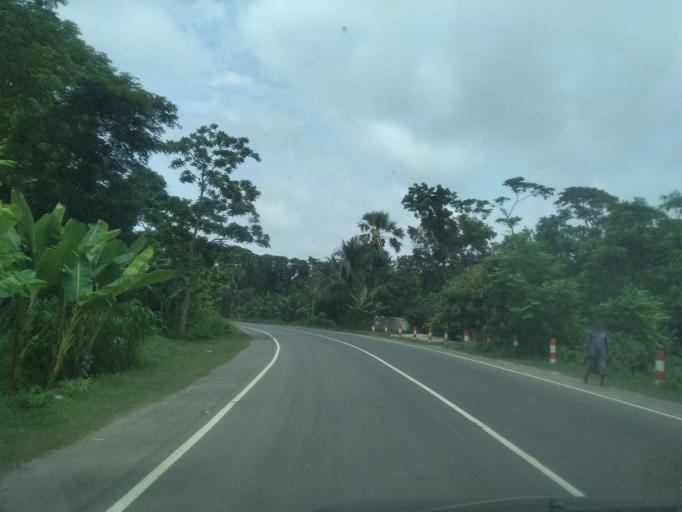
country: BD
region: Khulna
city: Kesabpur
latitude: 22.8155
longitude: 89.2489
